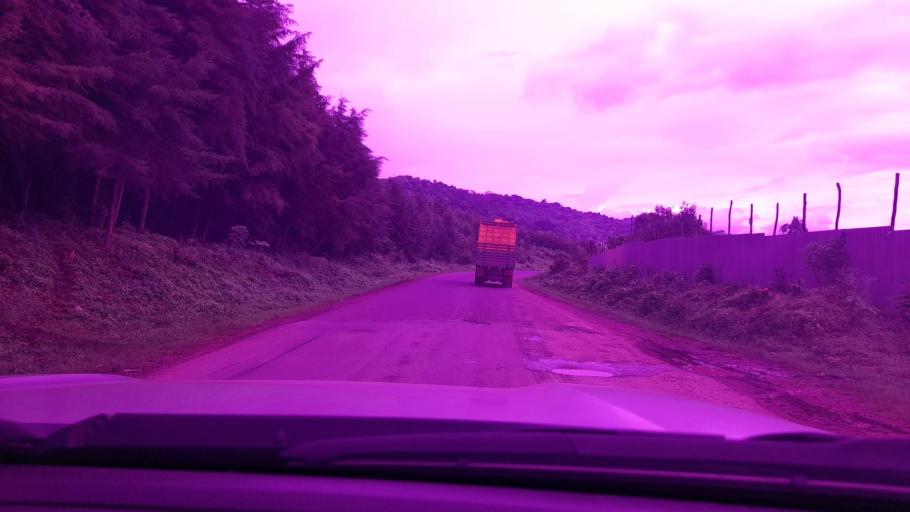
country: ET
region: Oromiya
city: Jima
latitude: 7.6624
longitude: 36.8755
